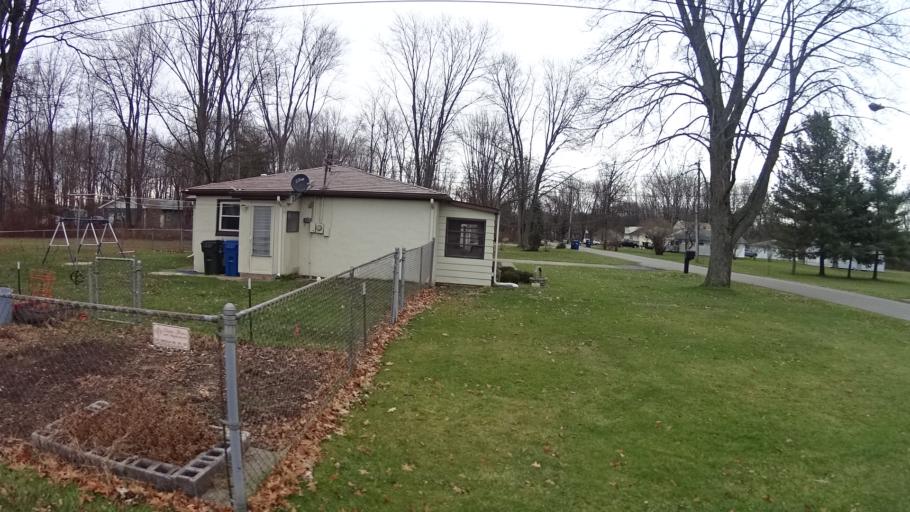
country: US
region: Ohio
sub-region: Lorain County
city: North Ridgeville
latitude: 41.3637
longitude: -82.0248
